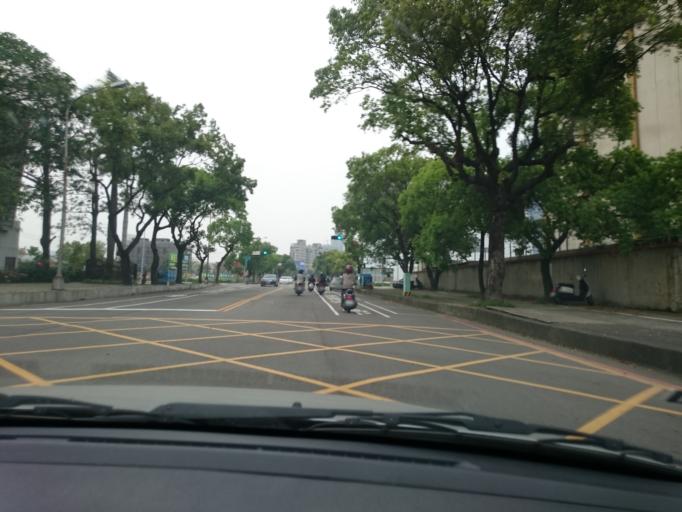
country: TW
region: Taiwan
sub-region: Taichung City
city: Taichung
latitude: 24.1577
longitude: 120.6342
